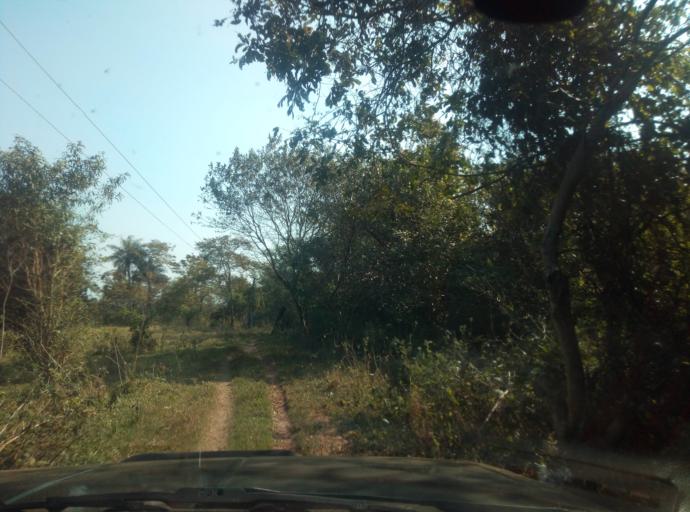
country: PY
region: Caaguazu
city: San Joaquin
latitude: -25.1571
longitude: -56.1267
